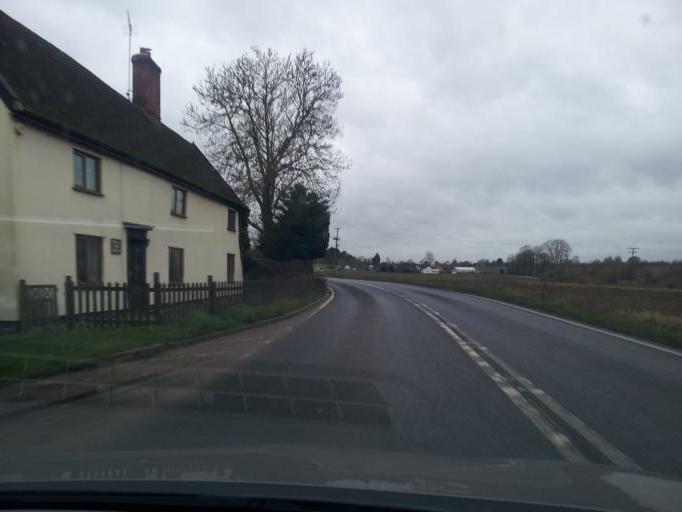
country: GB
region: England
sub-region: Suffolk
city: Botesdale
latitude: 52.3368
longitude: 0.9618
